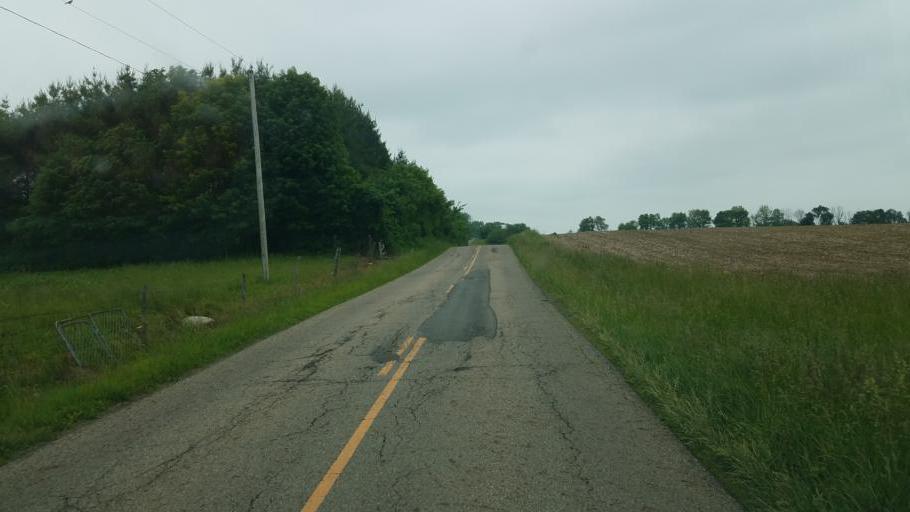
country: US
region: Ohio
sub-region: Knox County
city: Centerburg
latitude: 40.3327
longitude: -82.7269
